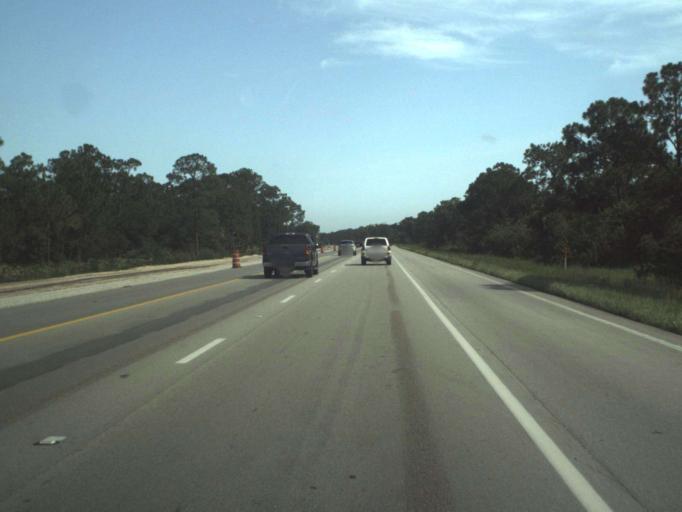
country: US
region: Florida
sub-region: Indian River County
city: West Vero Corridor
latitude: 27.6584
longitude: -80.5247
